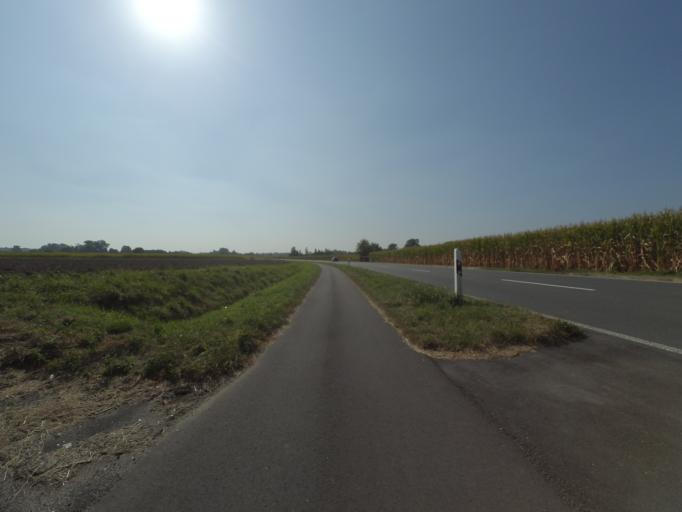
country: DE
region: North Rhine-Westphalia
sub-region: Regierungsbezirk Munster
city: Schoppingen
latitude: 52.0816
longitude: 7.2313
